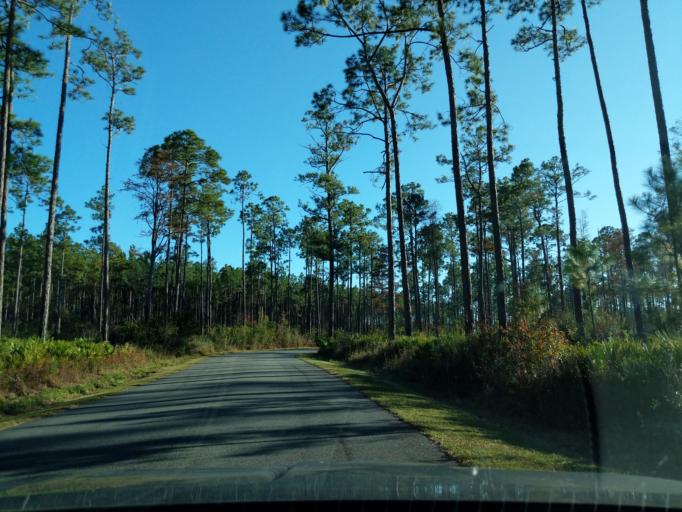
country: US
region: Georgia
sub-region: Charlton County
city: Folkston
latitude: 30.7126
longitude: -82.1413
